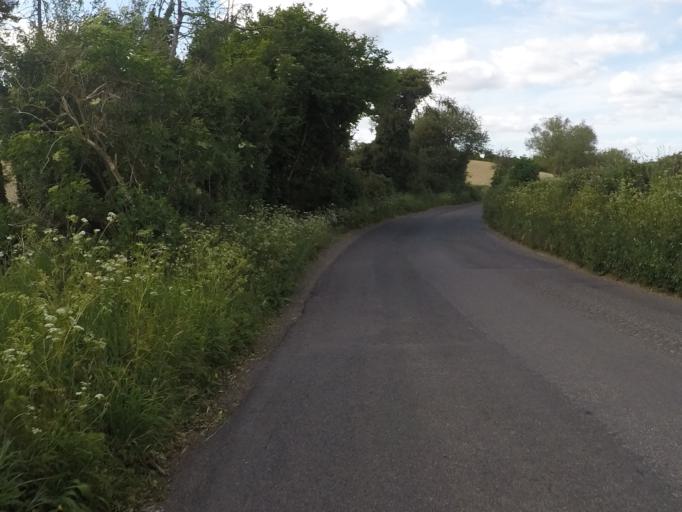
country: GB
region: England
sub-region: Oxfordshire
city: Witney
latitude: 51.8118
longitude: -1.5154
